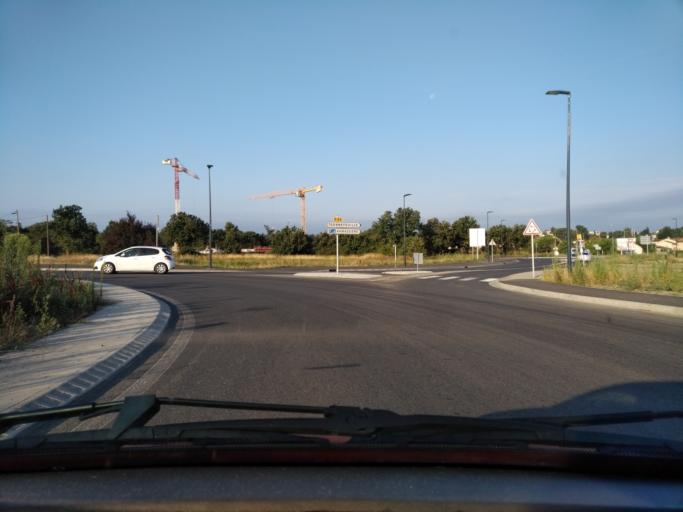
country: FR
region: Midi-Pyrenees
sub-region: Departement de la Haute-Garonne
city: Colomiers
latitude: 43.6067
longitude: 1.3532
